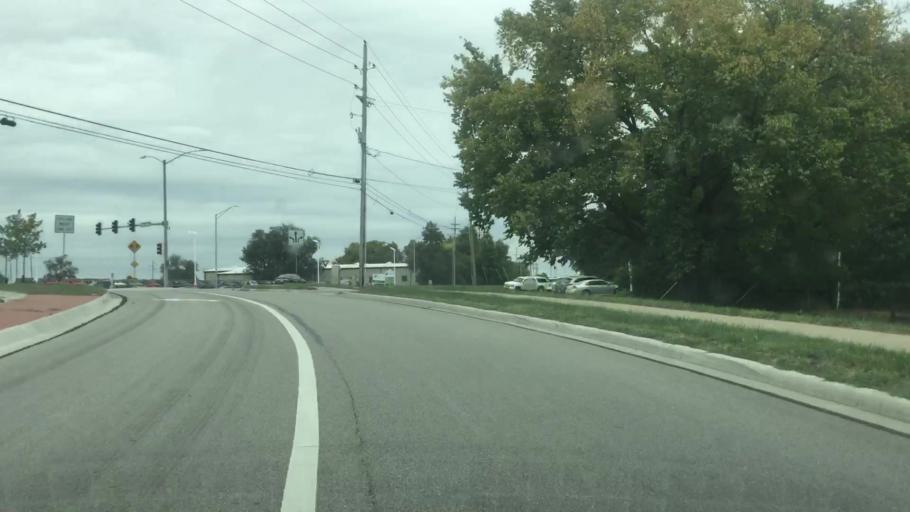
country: US
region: Kansas
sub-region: Johnson County
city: Lenexa
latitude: 38.9159
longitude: -94.7609
